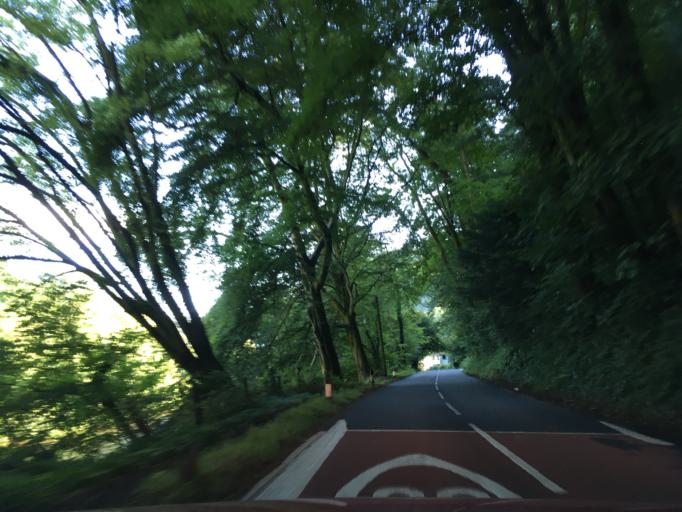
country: GB
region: Wales
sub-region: Monmouthshire
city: Monmouth
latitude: 51.7815
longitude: -2.6748
